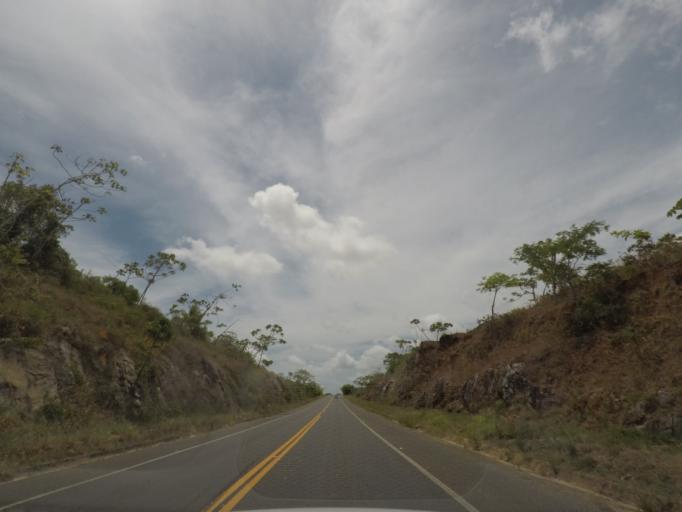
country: BR
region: Bahia
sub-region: Conde
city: Conde
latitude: -11.8079
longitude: -37.6315
